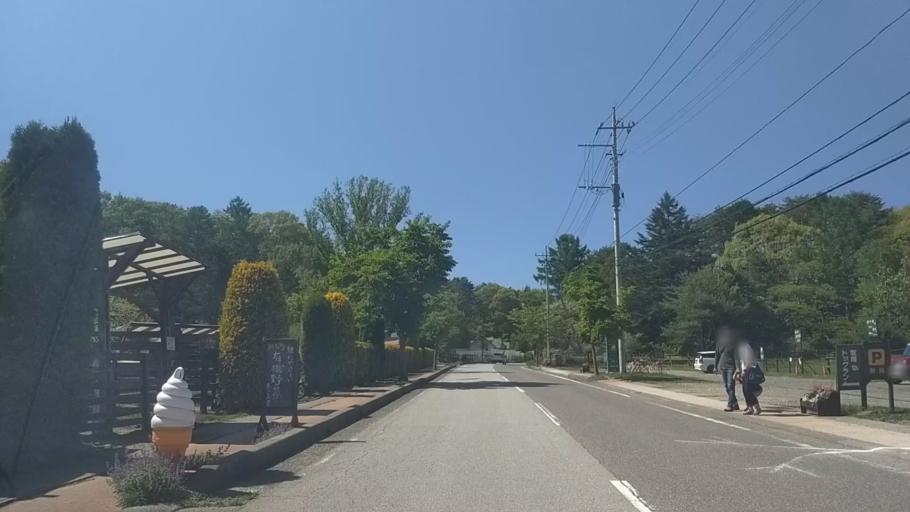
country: JP
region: Yamanashi
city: Nirasaki
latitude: 35.8964
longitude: 138.4378
